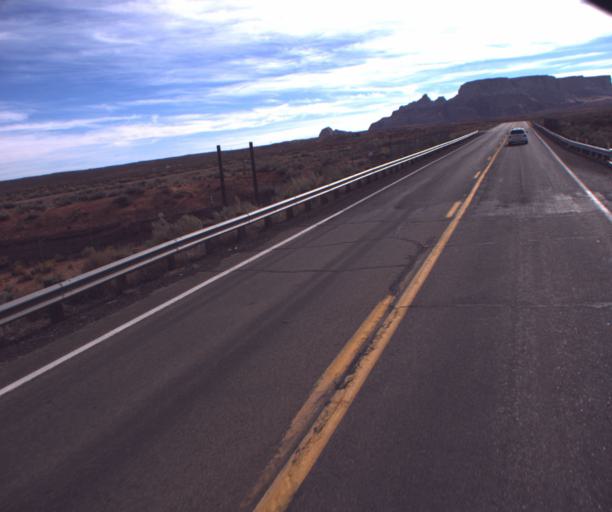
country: US
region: Arizona
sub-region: Coconino County
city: LeChee
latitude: 36.8815
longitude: -111.3505
